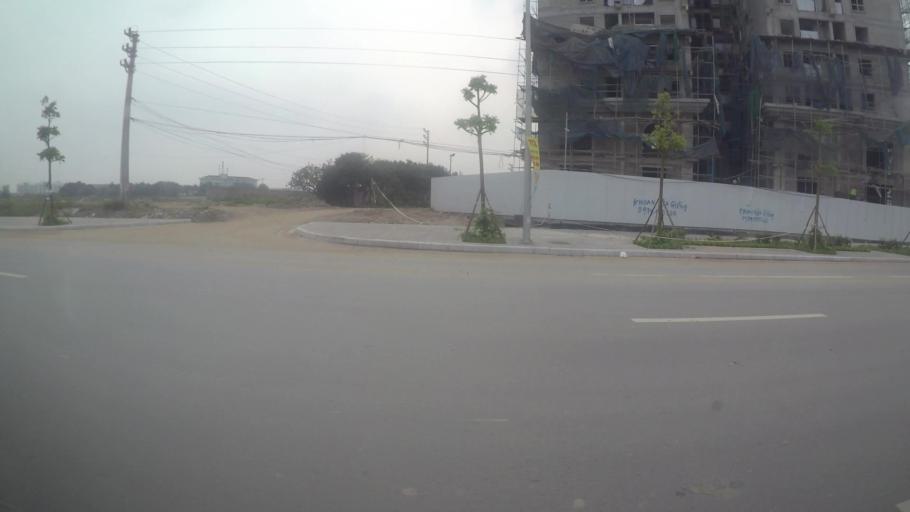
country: VN
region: Ha Noi
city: Cau Dien
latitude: 21.0474
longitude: 105.7358
